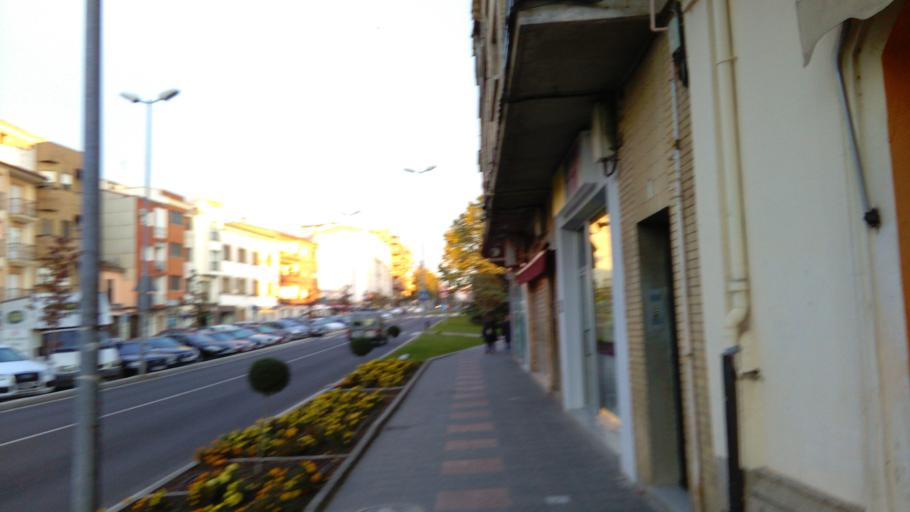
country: ES
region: Extremadura
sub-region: Provincia de Caceres
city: Coria
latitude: 39.9857
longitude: -6.5370
